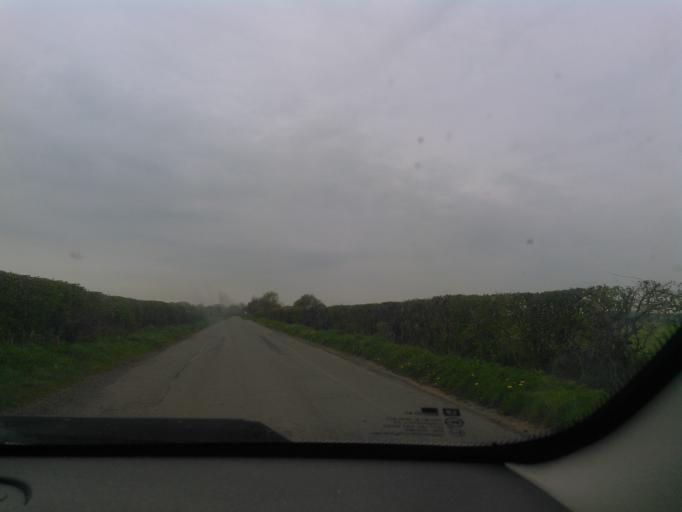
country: GB
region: England
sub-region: Shropshire
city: Stoke upon Tern
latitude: 52.7965
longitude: -2.5751
